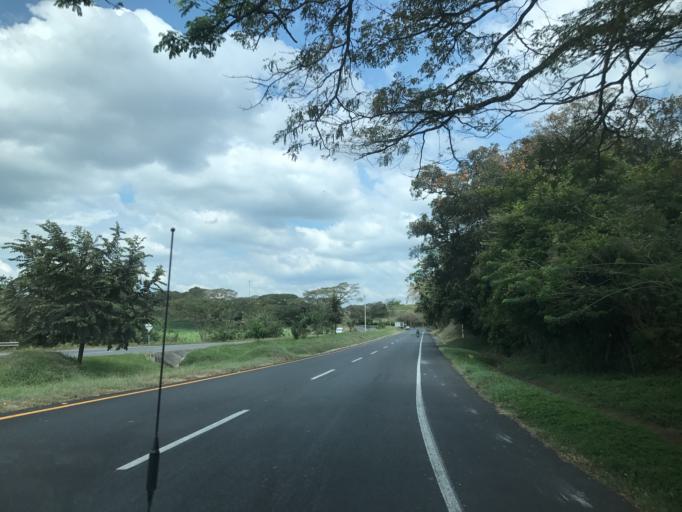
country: CO
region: Valle del Cauca
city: Obando
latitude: 4.6066
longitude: -75.9574
